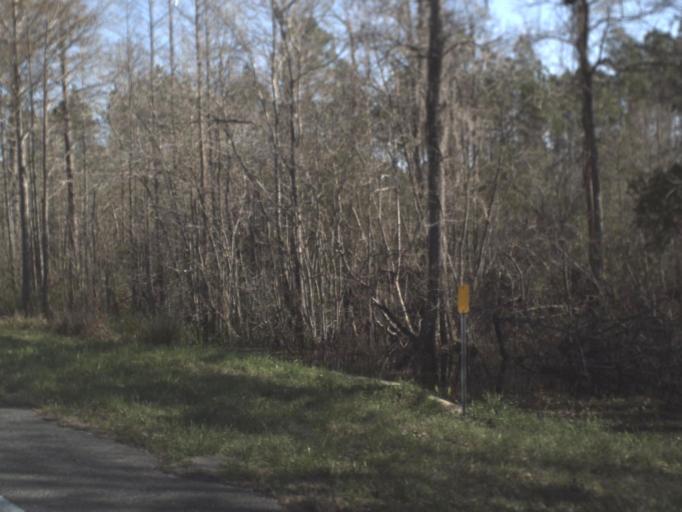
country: US
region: Florida
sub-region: Leon County
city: Woodville
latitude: 30.2304
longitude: -84.0426
